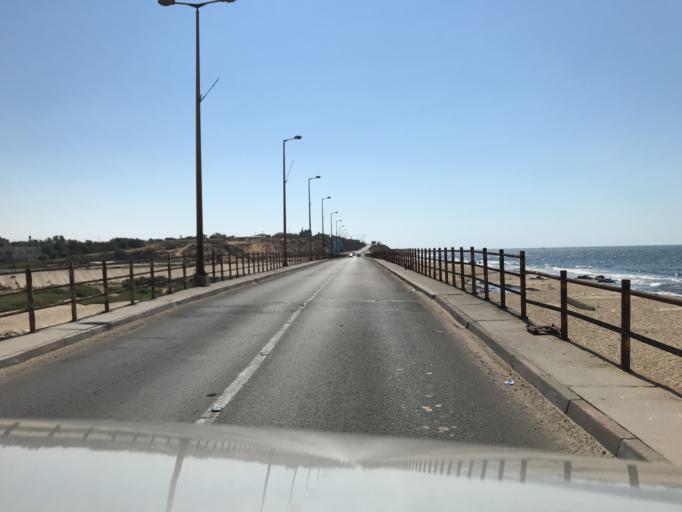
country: PS
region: Gaza Strip
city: An Nusayrat
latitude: 31.4645
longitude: 34.3768
